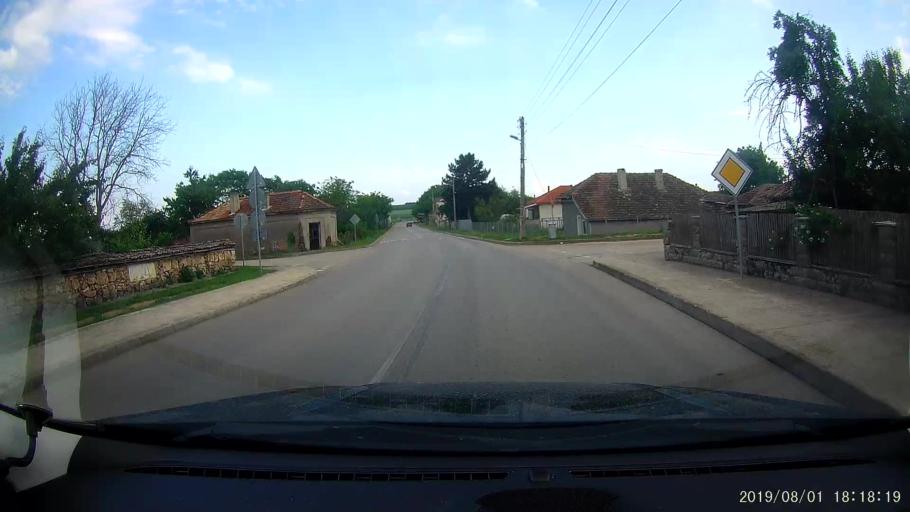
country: BG
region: Shumen
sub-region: Obshtina Kaolinovo
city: Kaolinovo
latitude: 43.6994
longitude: 27.0805
